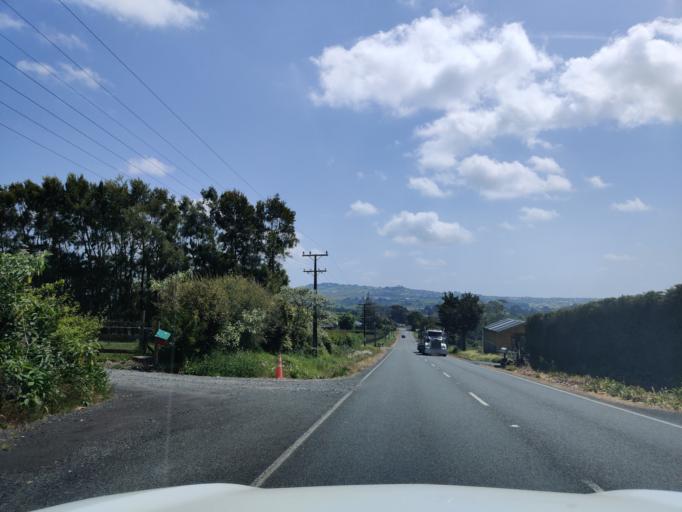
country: NZ
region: Auckland
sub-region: Auckland
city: Pukekohe East
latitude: -37.2137
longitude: 174.9415
